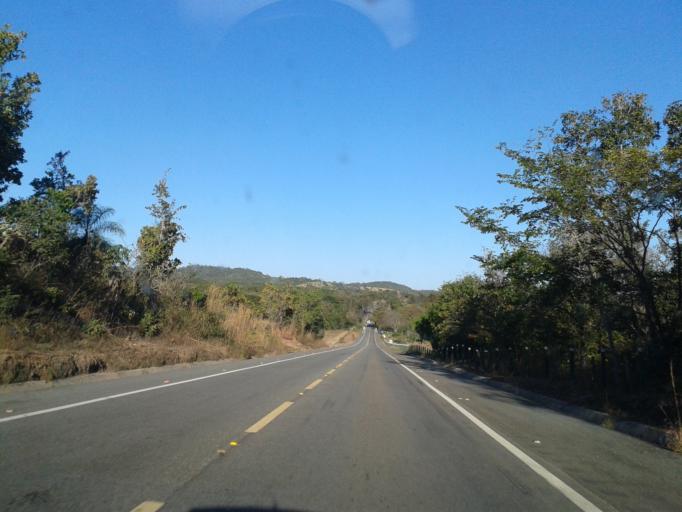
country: BR
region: Goias
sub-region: Goias
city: Goias
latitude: -15.7482
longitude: -50.1725
